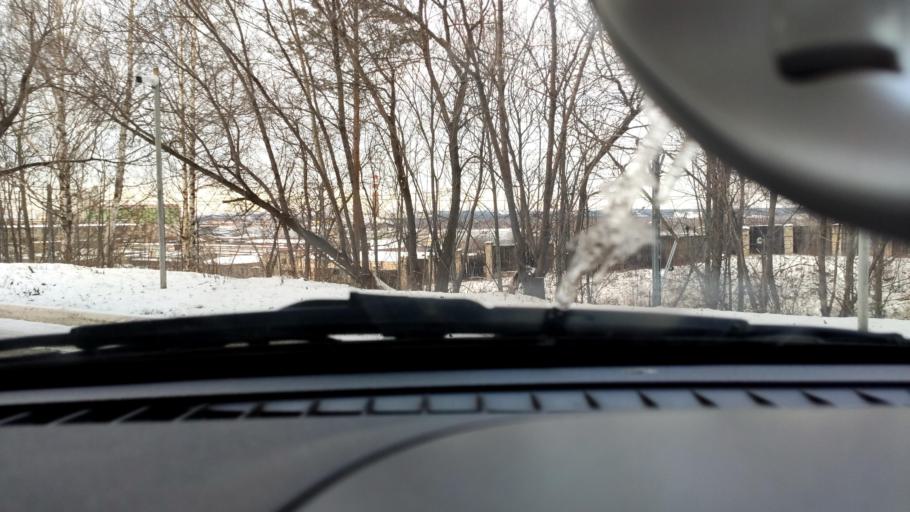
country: RU
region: Perm
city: Perm
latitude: 58.0112
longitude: 56.2002
